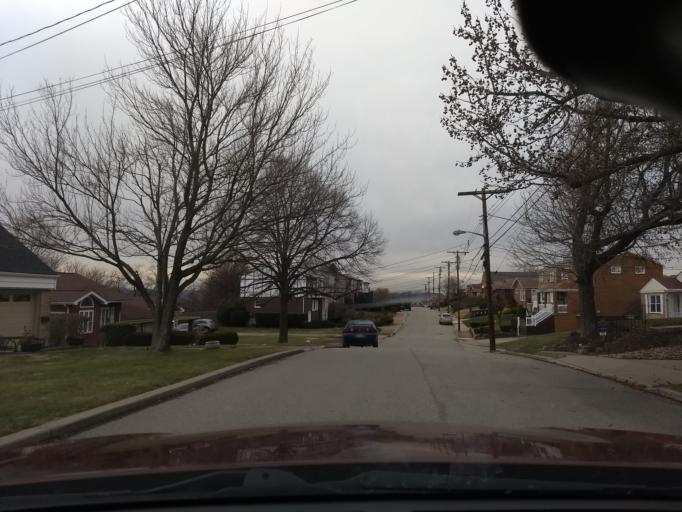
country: US
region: Pennsylvania
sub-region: Allegheny County
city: Homestead
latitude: 40.4183
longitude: -79.9387
